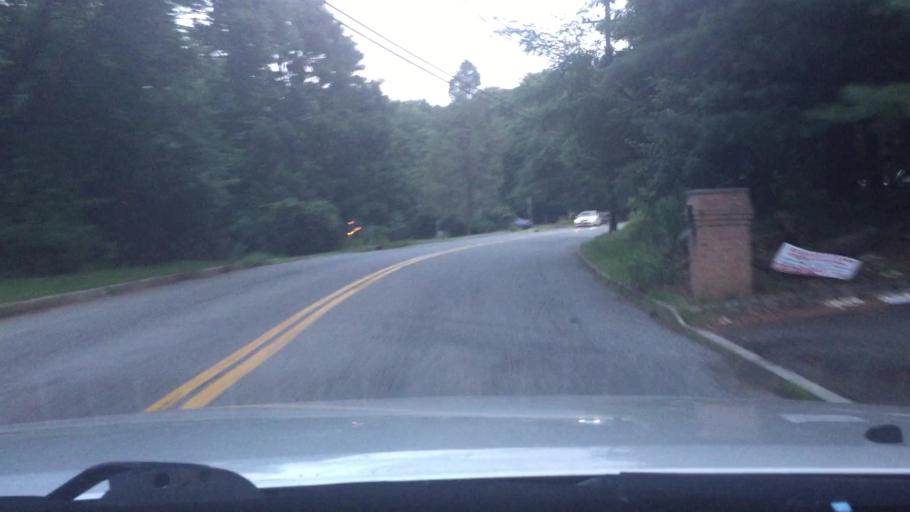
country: US
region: New Jersey
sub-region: Middlesex County
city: Milltown
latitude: 40.4382
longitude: -74.4650
